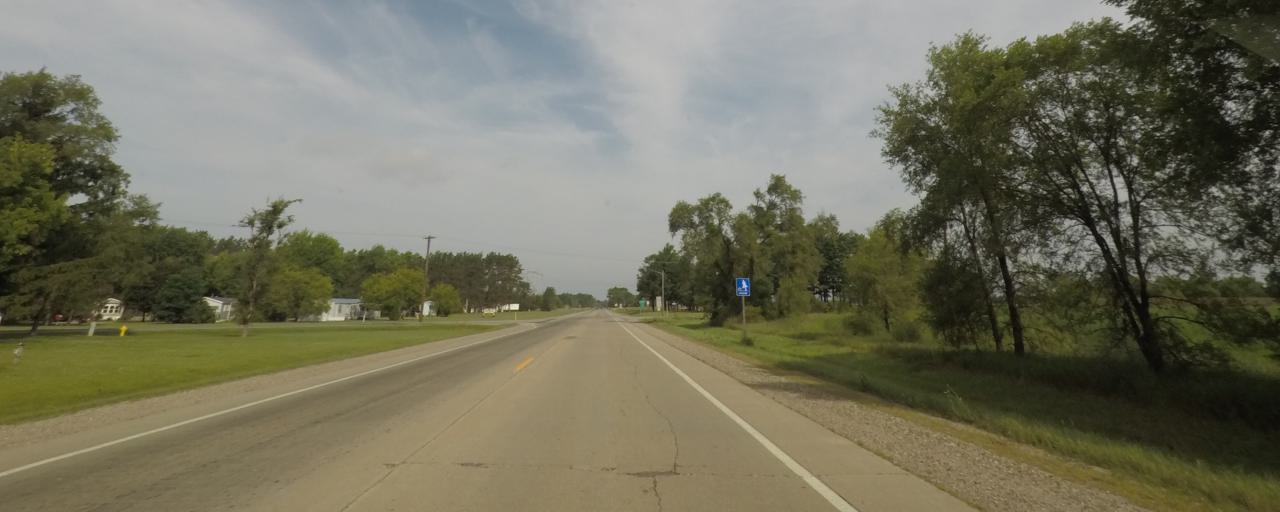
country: US
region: Wisconsin
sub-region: Portage County
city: Plover
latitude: 44.4369
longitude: -89.5278
